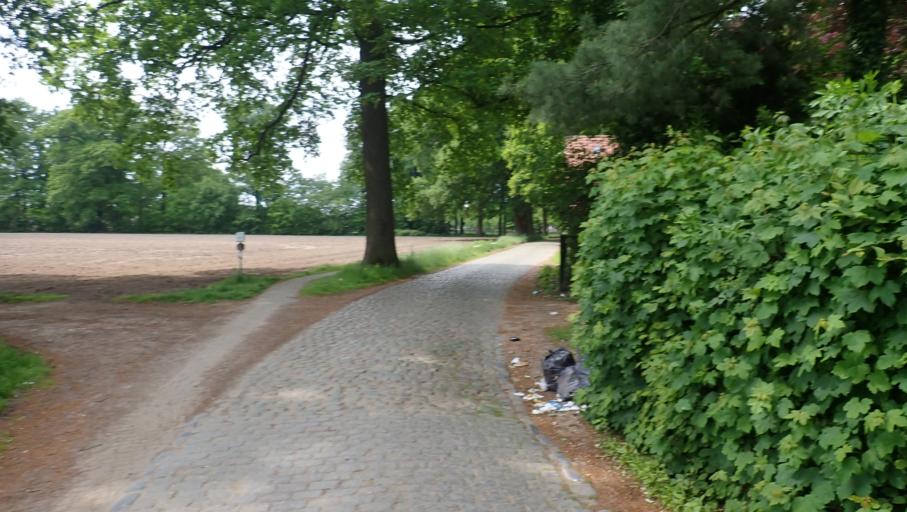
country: BE
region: Flanders
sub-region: Provincie Antwerpen
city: Oostmalle
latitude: 51.3056
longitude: 4.6971
